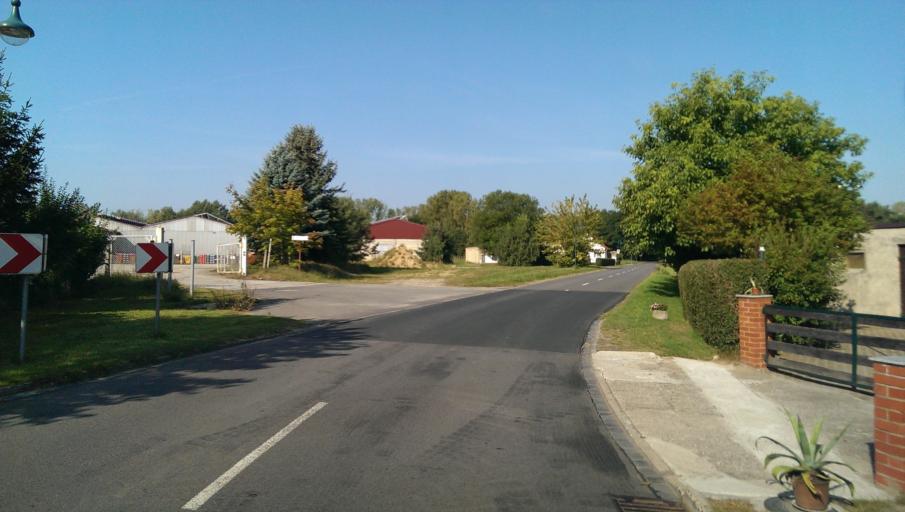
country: DE
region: Saxony-Anhalt
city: Kropstadt
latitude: 51.9670
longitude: 12.7438
